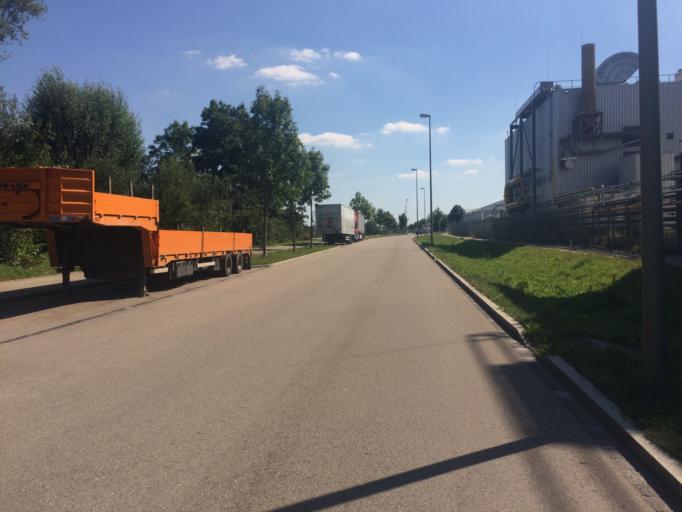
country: DE
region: Bavaria
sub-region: Swabia
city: Augsburg
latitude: 48.4005
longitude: 10.9382
